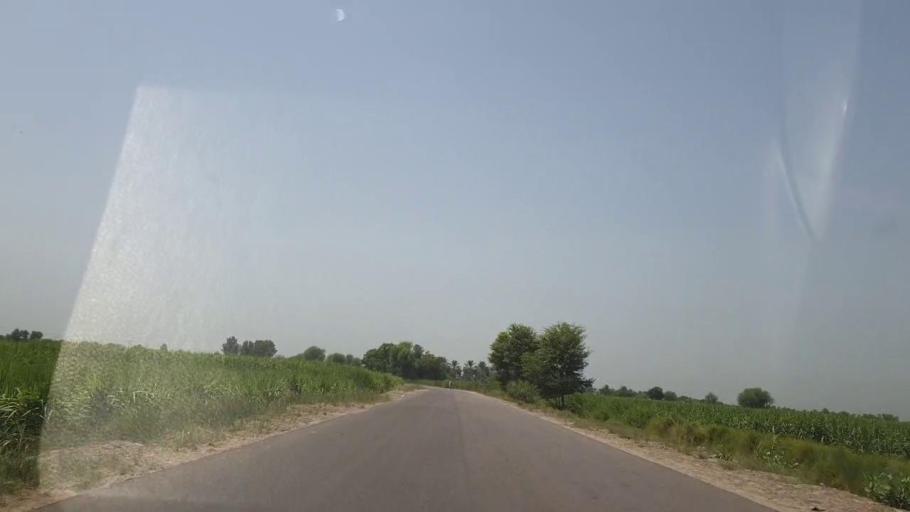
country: PK
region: Sindh
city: Ranipur
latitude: 27.2940
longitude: 68.6046
